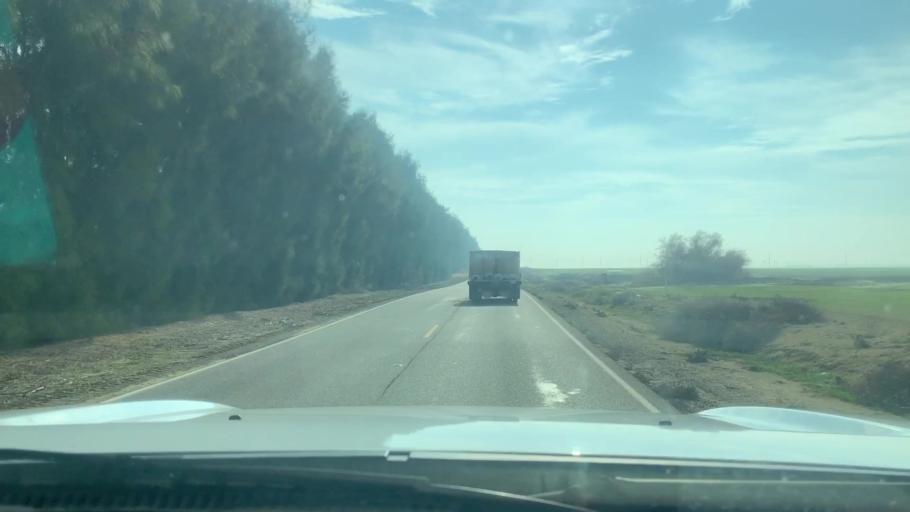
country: US
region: California
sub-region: Kern County
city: Lost Hills
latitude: 35.5076
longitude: -119.7458
